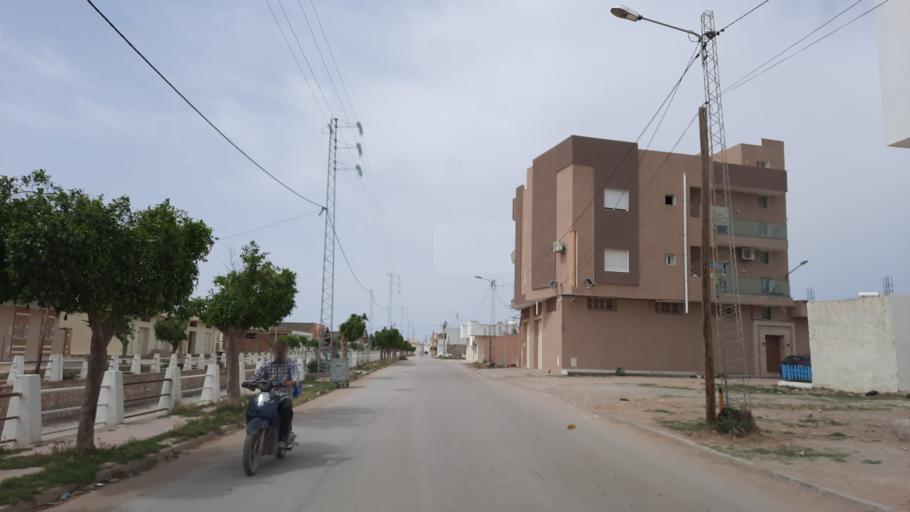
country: TN
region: Al Mahdiyah
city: El Jem
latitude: 35.3031
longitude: 10.7048
